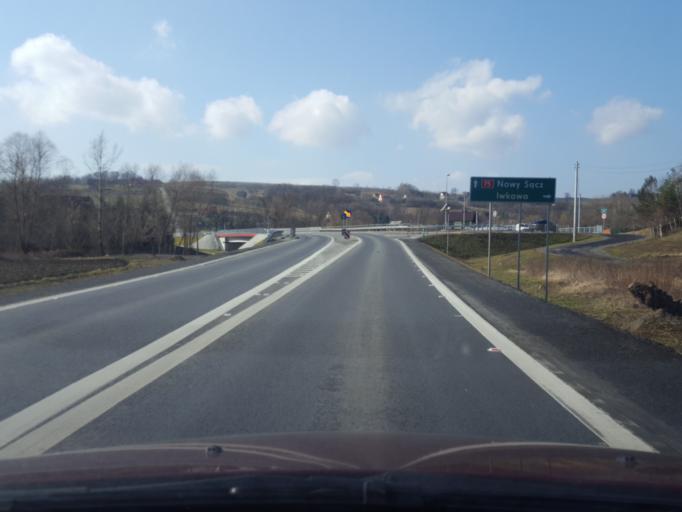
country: PL
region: Lesser Poland Voivodeship
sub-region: Powiat nowosadecki
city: Lososina Dolna
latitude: 49.7663
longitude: 20.6344
